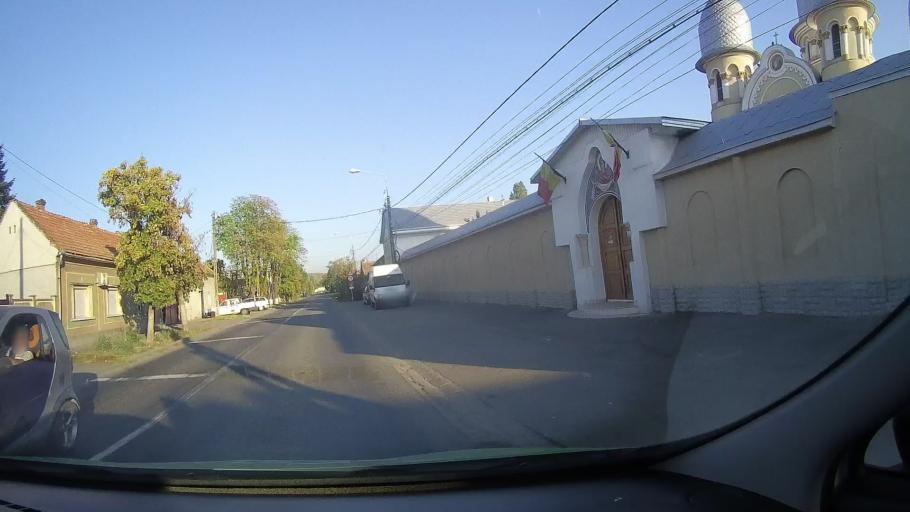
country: RO
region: Bihor
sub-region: Comuna Santandrei
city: Santandrei
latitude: 47.1035
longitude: 21.8874
